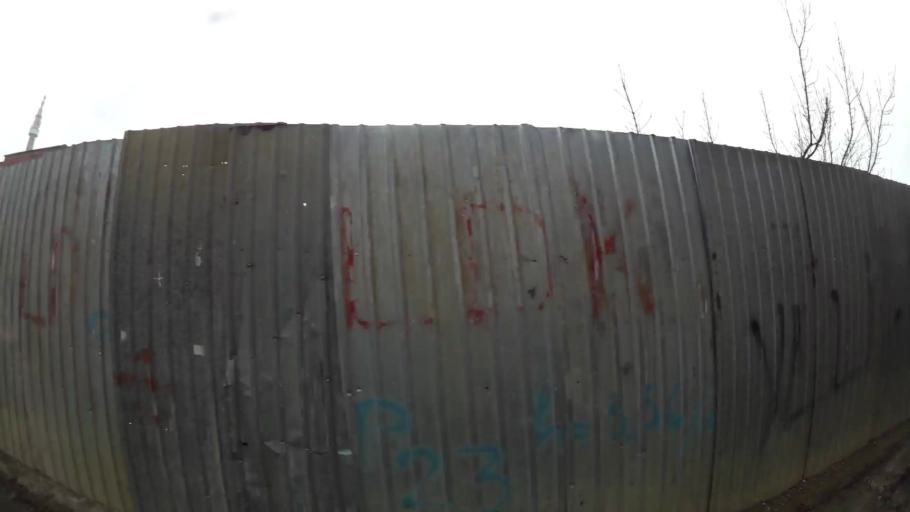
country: XK
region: Pristina
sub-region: Komuna e Prishtines
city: Pristina
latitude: 42.6799
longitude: 21.1660
